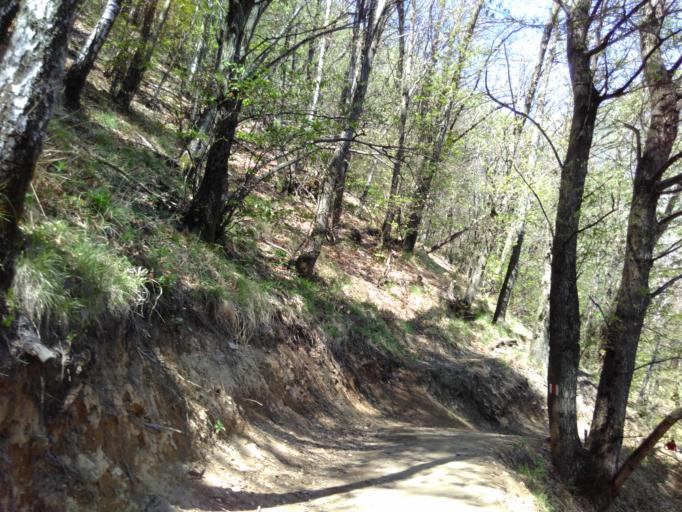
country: CH
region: Ticino
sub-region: Bellinzona District
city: Sementina
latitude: 46.1906
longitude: 8.9754
